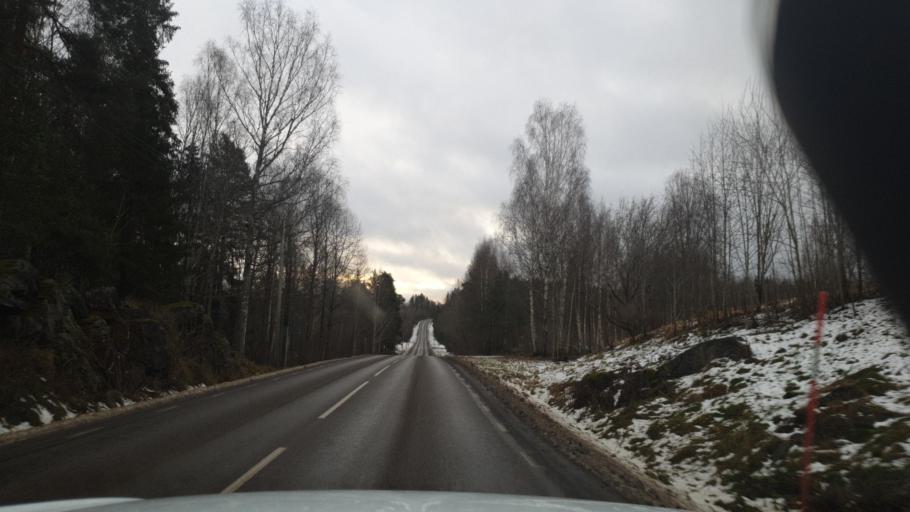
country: SE
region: Vaermland
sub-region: Eda Kommun
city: Amotfors
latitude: 59.7564
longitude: 12.3595
